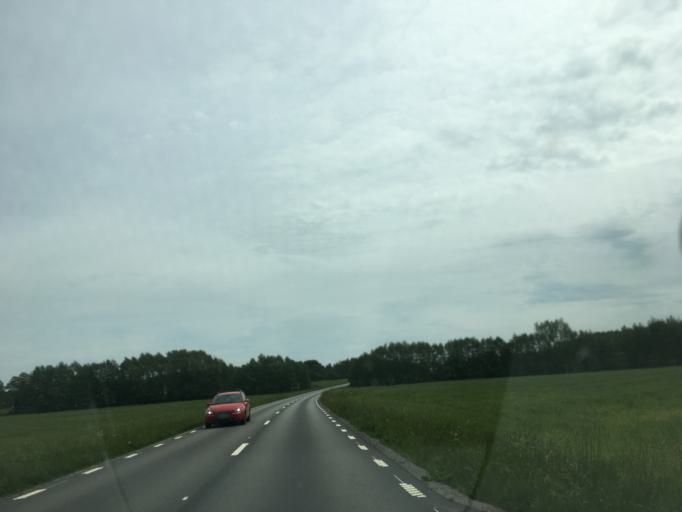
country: SE
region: Skane
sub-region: Sjobo Kommun
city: Blentarp
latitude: 55.6003
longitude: 13.5929
